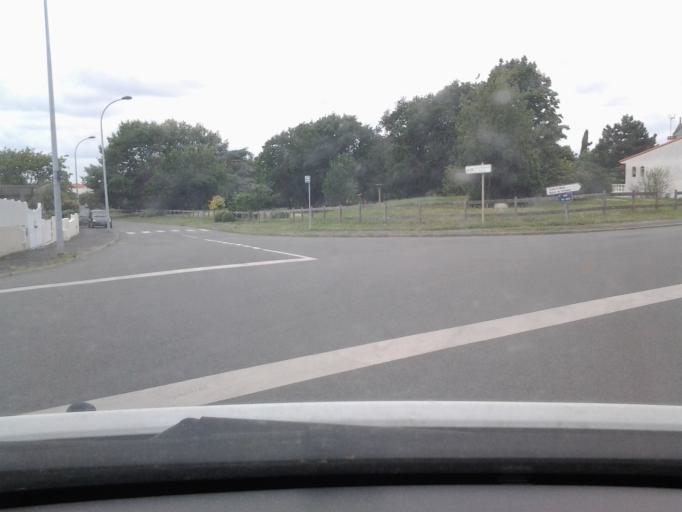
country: FR
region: Pays de la Loire
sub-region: Departement de la Vendee
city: La Roche-sur-Yon
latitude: 46.6629
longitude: -1.4464
